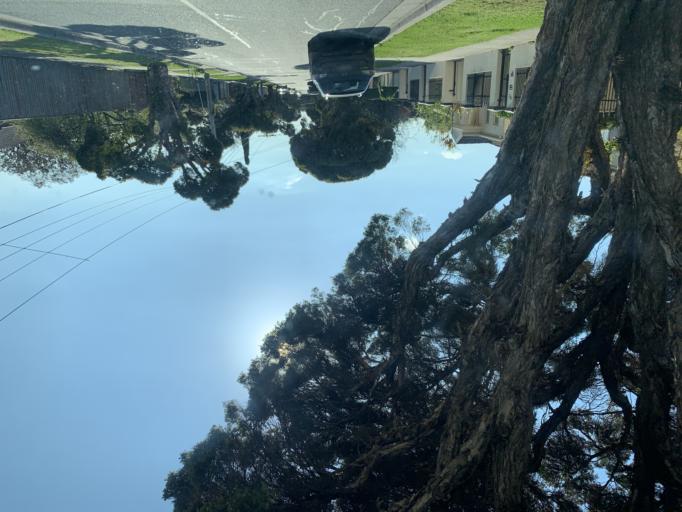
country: AU
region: Victoria
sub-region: Kingston
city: Mordialloc
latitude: -37.9956
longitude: 145.0920
